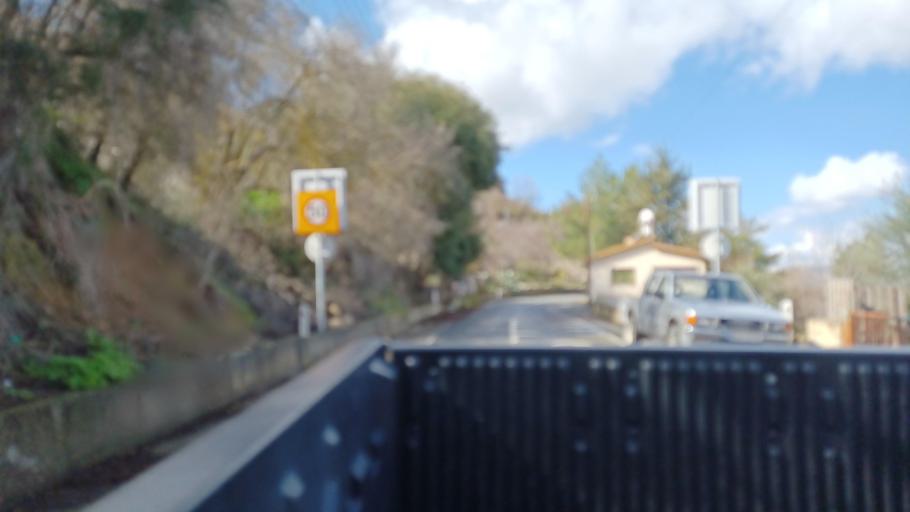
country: CY
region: Limassol
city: Pachna
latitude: 34.7791
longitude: 32.7357
